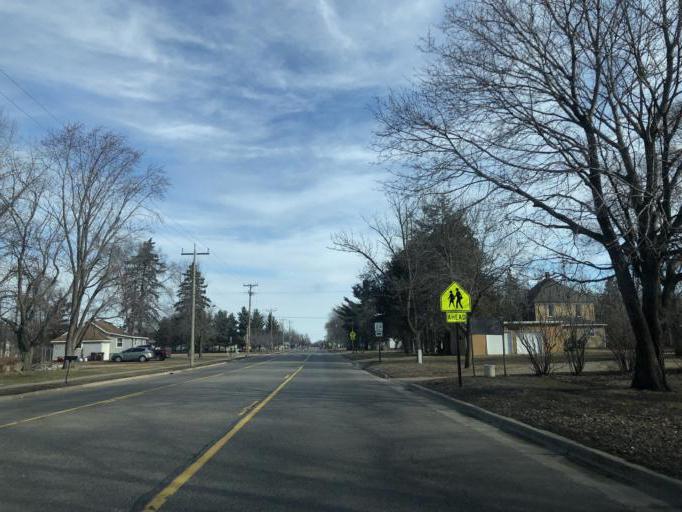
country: US
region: Minnesota
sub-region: Sherburne County
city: Becker
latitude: 45.3927
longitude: -93.8704
